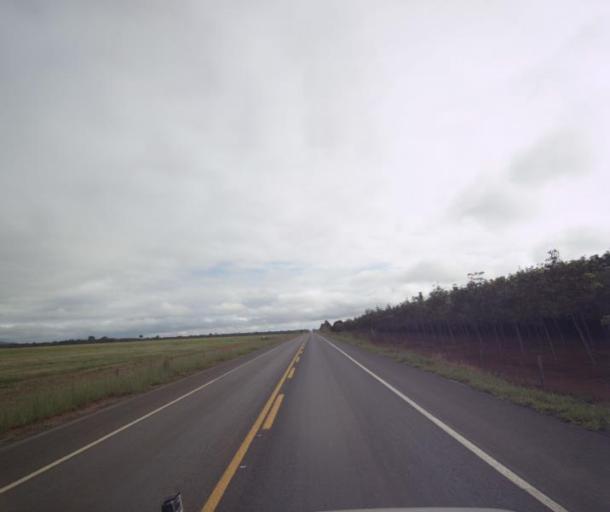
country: BR
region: Goias
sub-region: Padre Bernardo
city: Padre Bernardo
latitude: -15.3764
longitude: -48.6454
